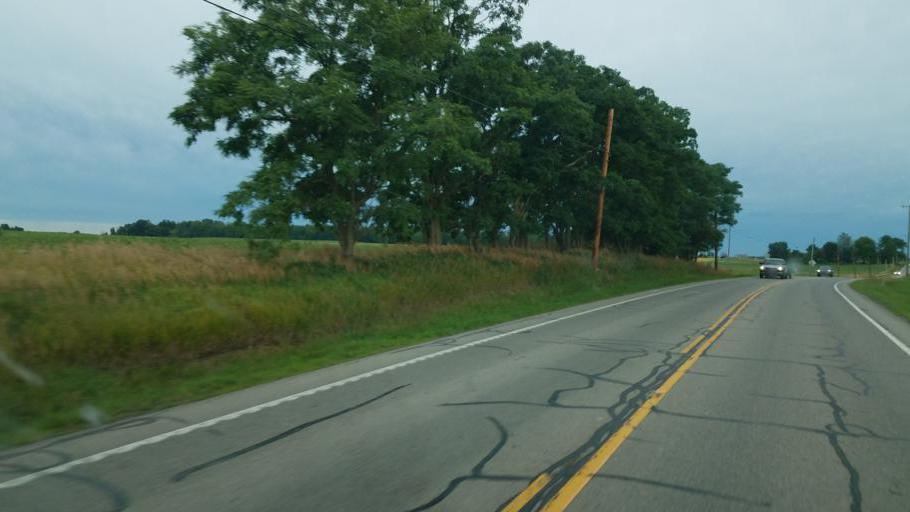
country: US
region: Ohio
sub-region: Huron County
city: Greenwich
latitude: 40.9401
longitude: -82.4948
